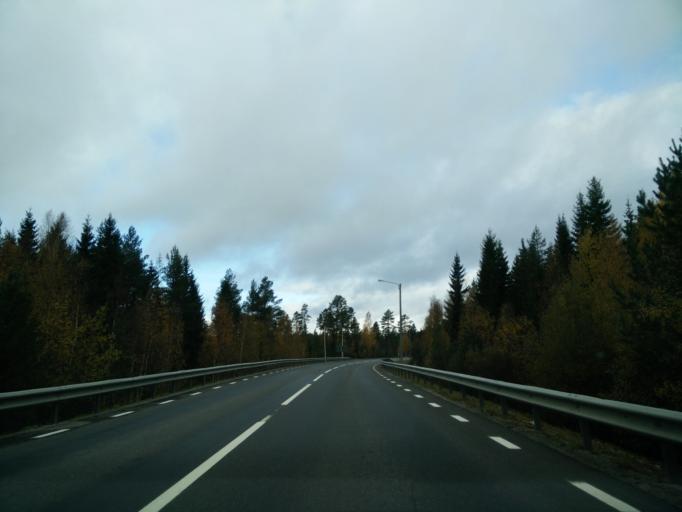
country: SE
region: Jaemtland
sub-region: Braecke Kommun
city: Braecke
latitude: 62.3953
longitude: 15.2252
